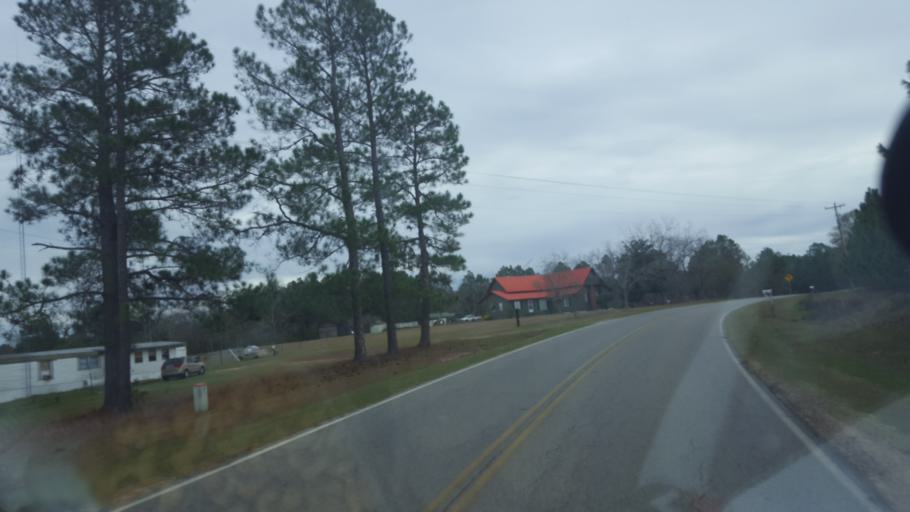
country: US
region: Georgia
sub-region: Ben Hill County
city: Fitzgerald
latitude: 31.7554
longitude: -83.3387
